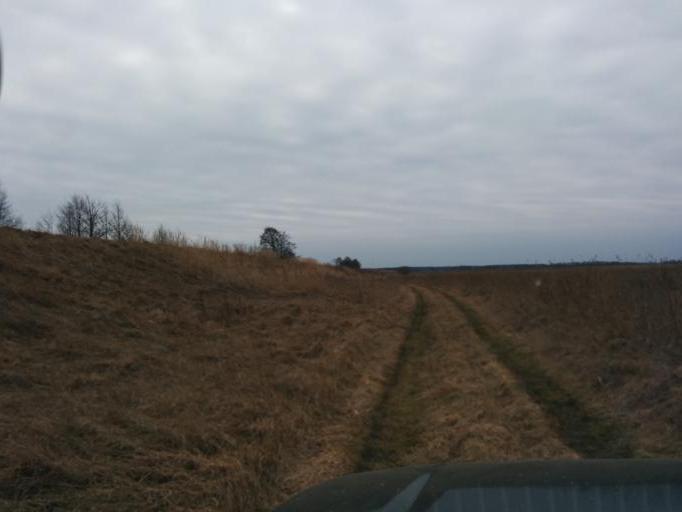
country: LV
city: Tireli
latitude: 56.9087
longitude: 23.6262
